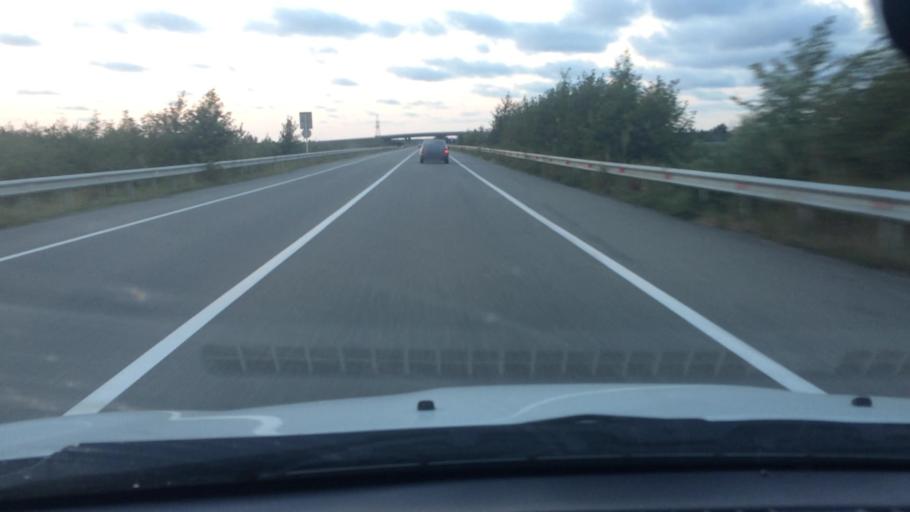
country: GE
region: Ajaria
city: Ochkhamuri
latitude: 41.8952
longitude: 41.8014
